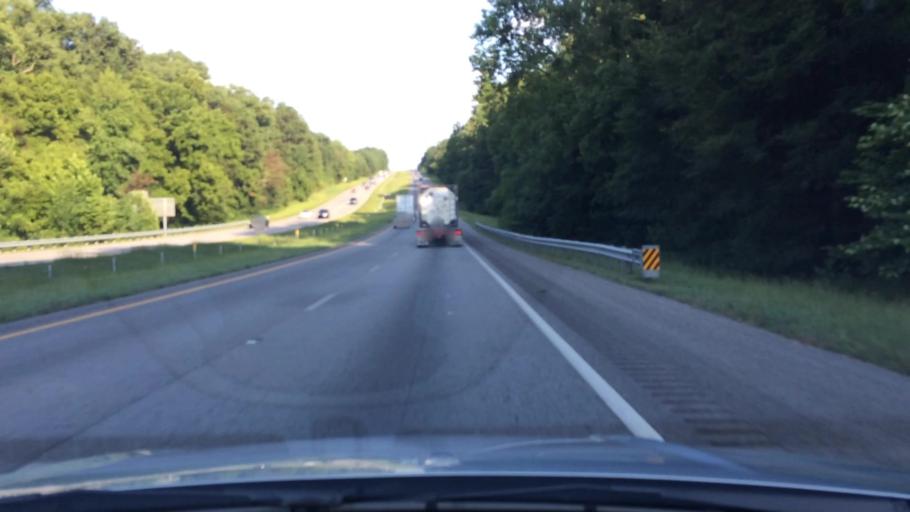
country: US
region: South Carolina
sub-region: Laurens County
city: Clinton
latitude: 34.4870
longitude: -81.8329
